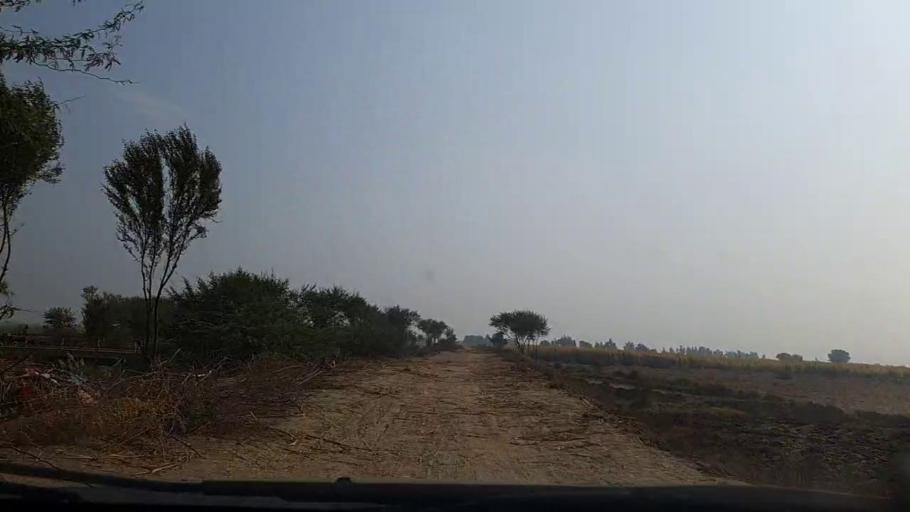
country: PK
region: Sindh
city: Sanghar
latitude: 26.0436
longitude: 68.9916
